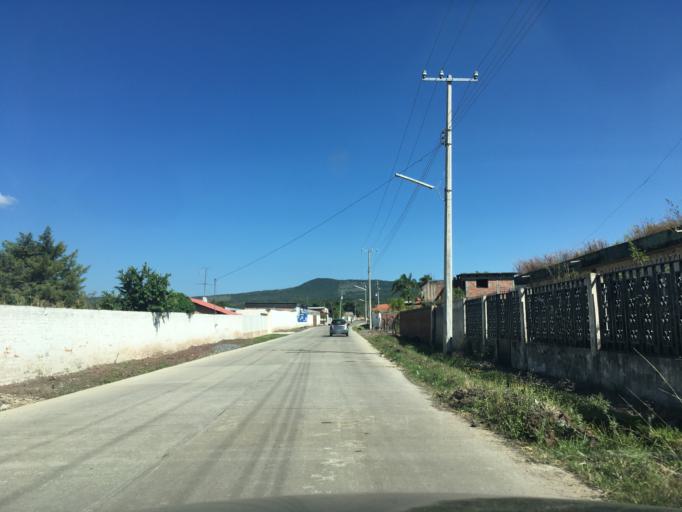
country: MX
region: Mexico
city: Tlazazalca
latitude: 19.9734
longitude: -102.1195
